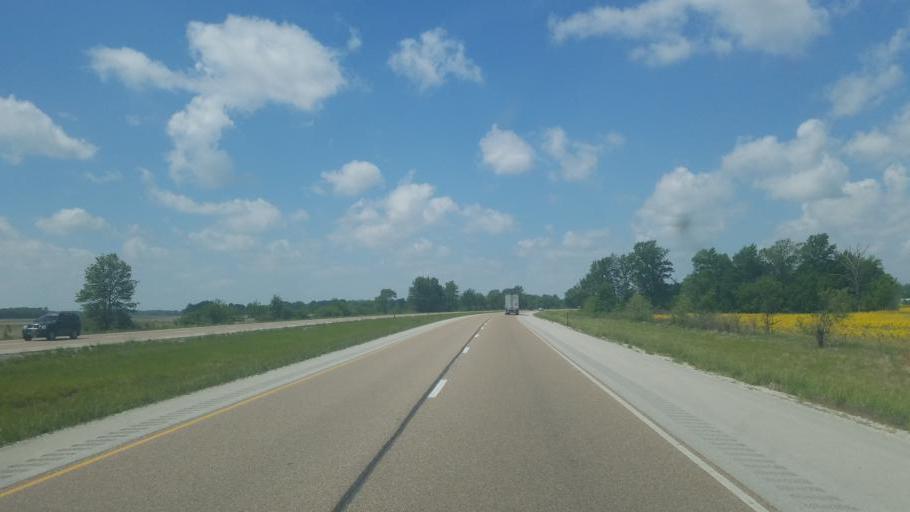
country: US
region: Illinois
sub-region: Cumberland County
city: Greenup
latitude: 39.2779
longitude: -88.0834
